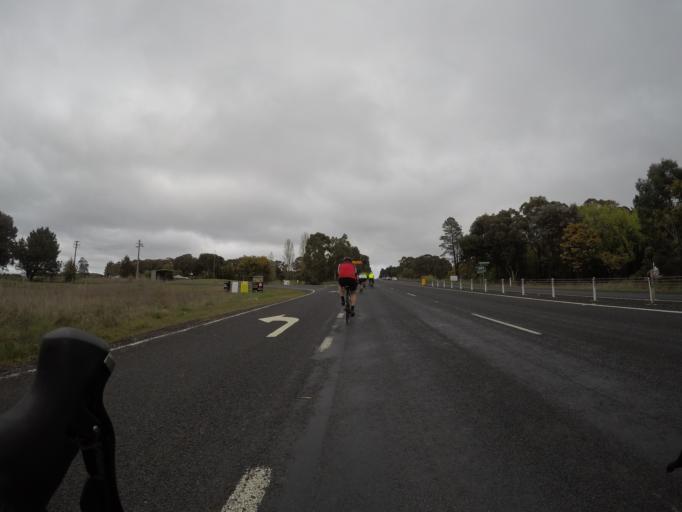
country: AU
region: New South Wales
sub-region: Lithgow
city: Portland
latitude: -33.4340
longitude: 149.8737
